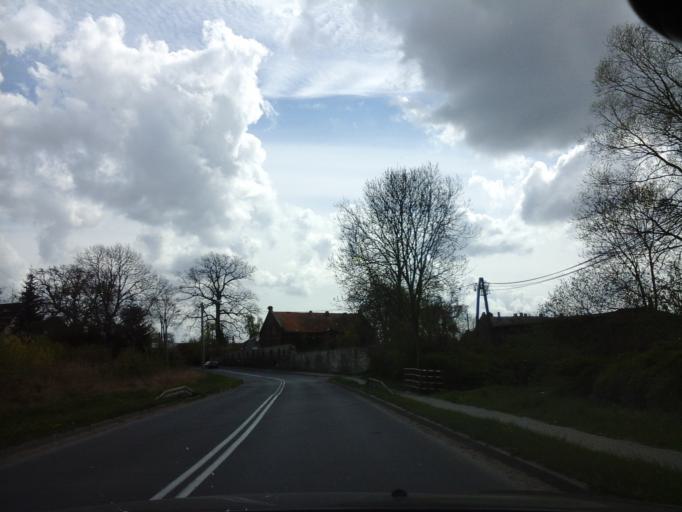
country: PL
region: West Pomeranian Voivodeship
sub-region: Powiat stargardzki
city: Suchan
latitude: 53.2290
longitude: 15.2976
